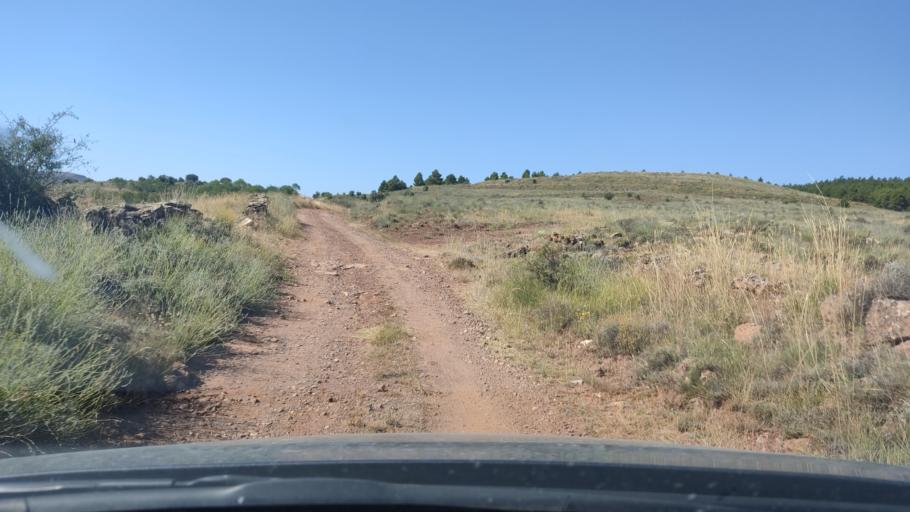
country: ES
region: Aragon
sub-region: Provincia de Teruel
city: Monforte de Moyuela
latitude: 41.0469
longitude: -1.0331
